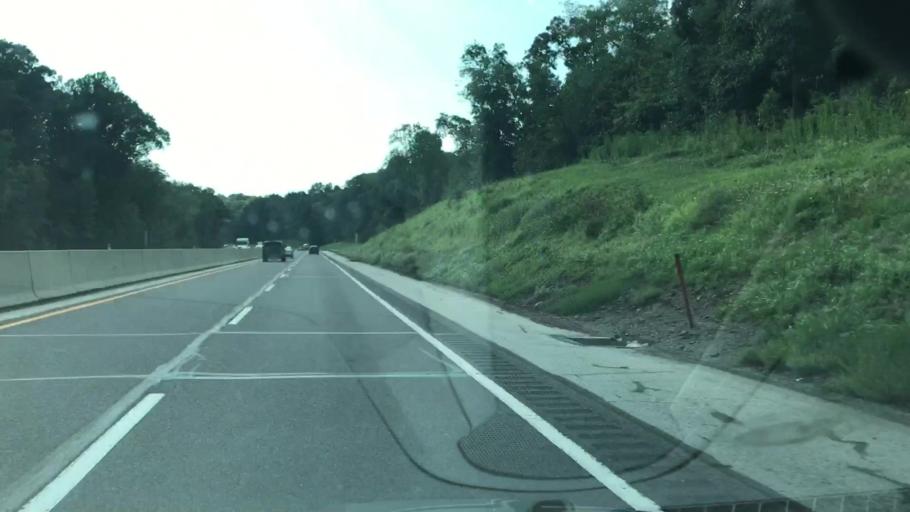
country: US
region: Pennsylvania
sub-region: Lebanon County
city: Cornwall
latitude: 40.2272
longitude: -76.4851
